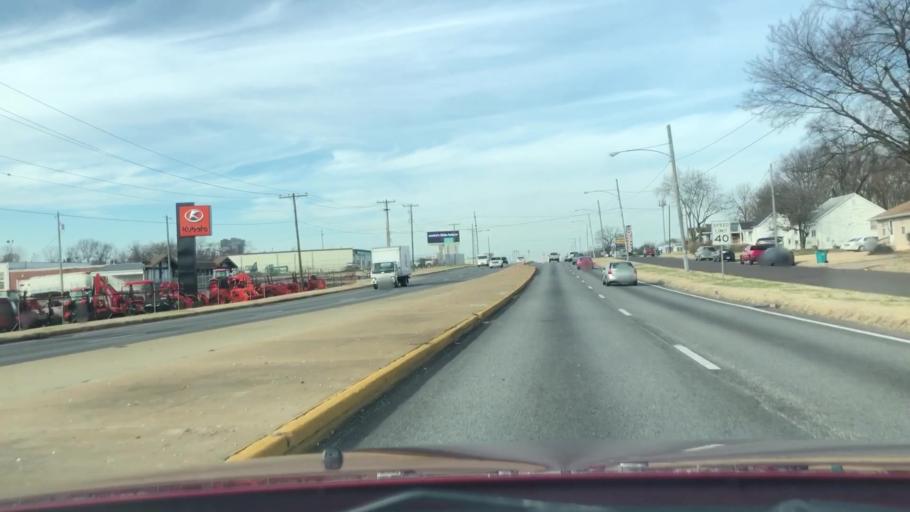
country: US
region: Missouri
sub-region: Greene County
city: Springfield
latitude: 37.2147
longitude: -93.2638
